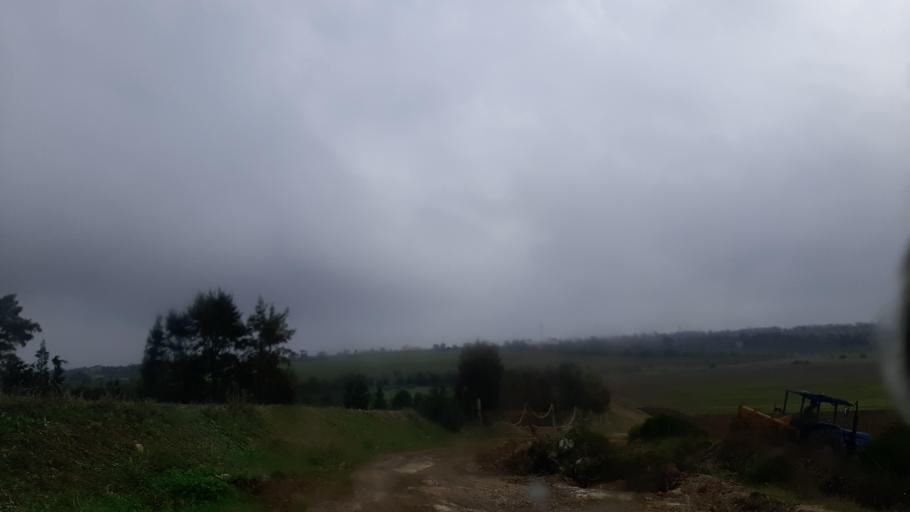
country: TN
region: Nabul
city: Qulaybiyah
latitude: 36.8275
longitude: 11.0355
